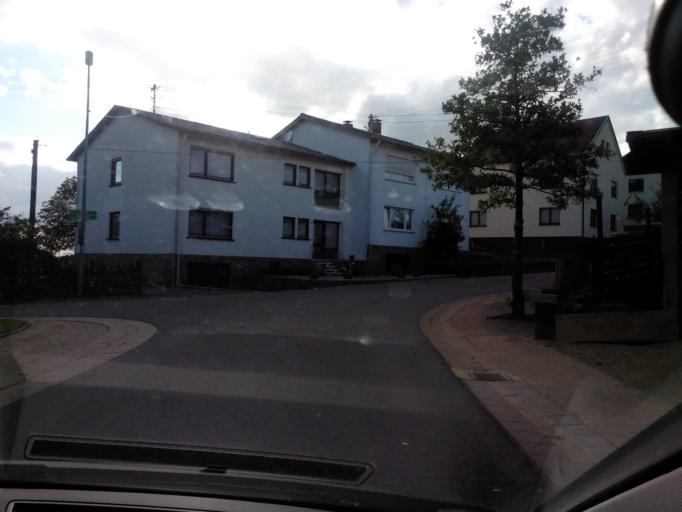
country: DE
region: Saarland
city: Merzig
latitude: 49.3776
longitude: 6.5926
